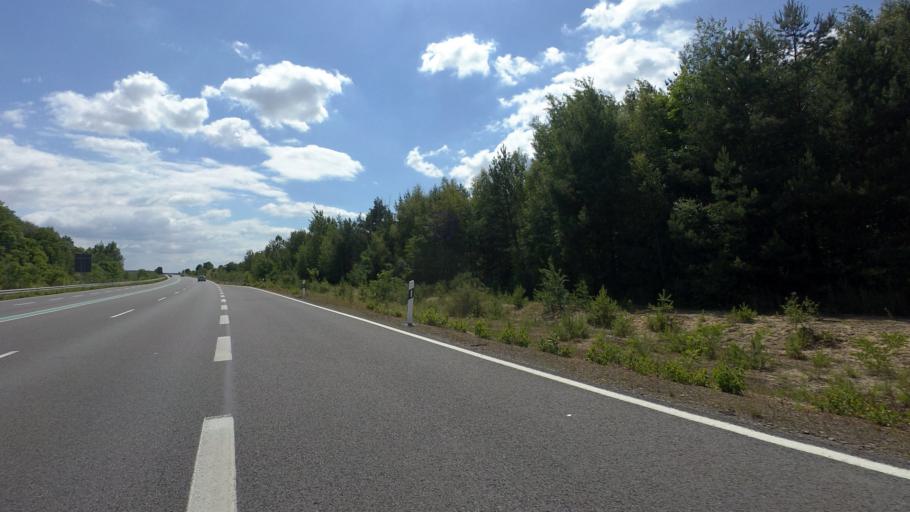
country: DE
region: Brandenburg
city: Senftenberg
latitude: 51.5246
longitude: 13.9649
